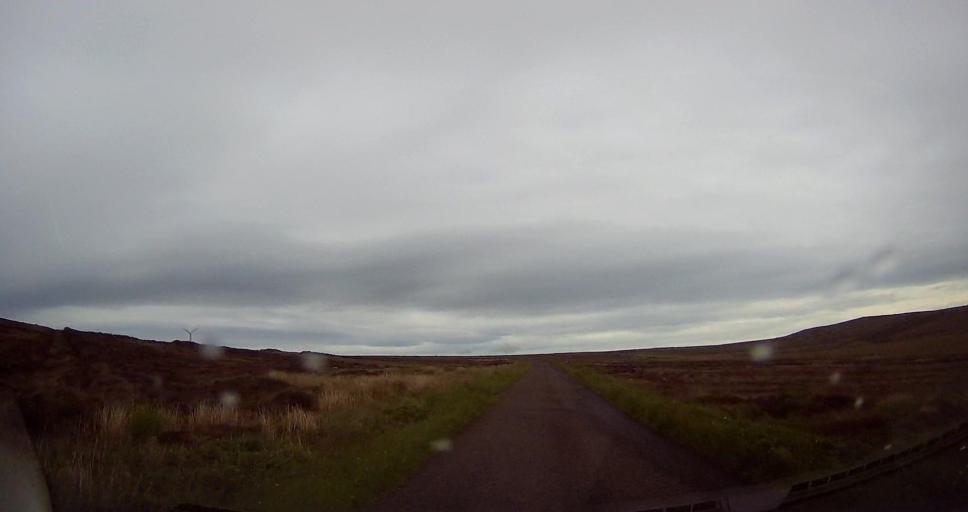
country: GB
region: Scotland
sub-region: Orkney Islands
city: Stromness
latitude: 59.0965
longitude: -3.1555
